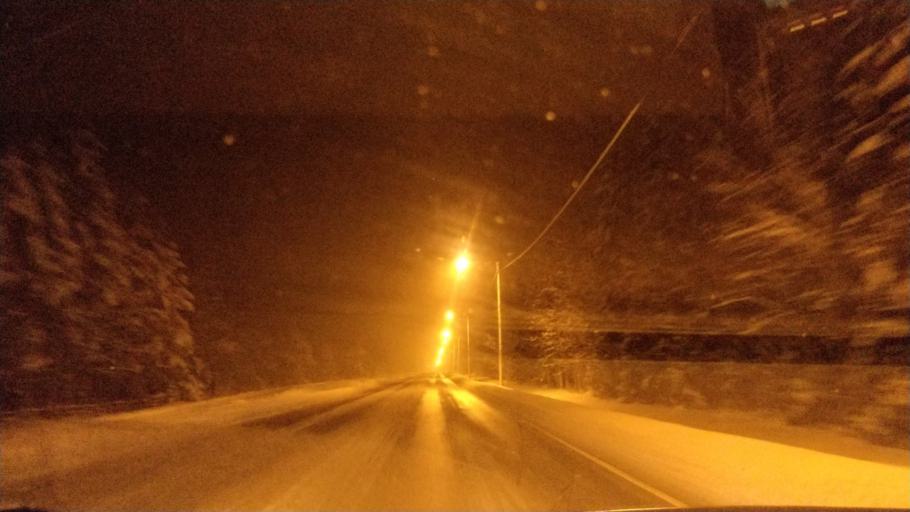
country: FI
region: Lapland
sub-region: Rovaniemi
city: Rovaniemi
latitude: 66.4135
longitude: 25.4089
